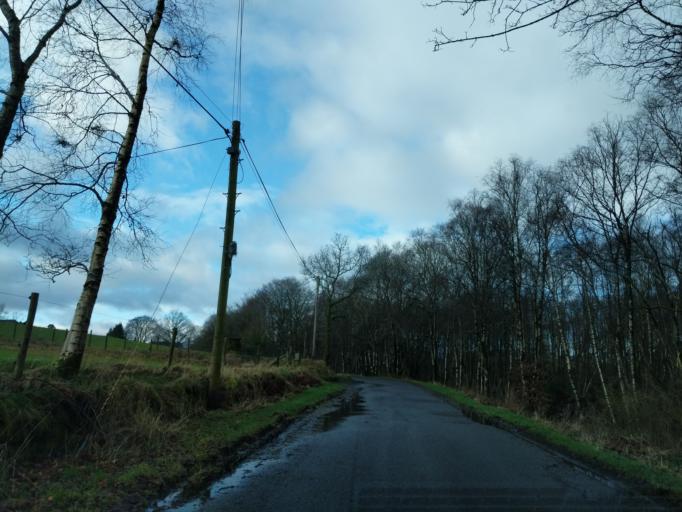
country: GB
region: Scotland
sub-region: Dumfries and Galloway
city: Moffat
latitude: 55.3189
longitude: -3.4242
